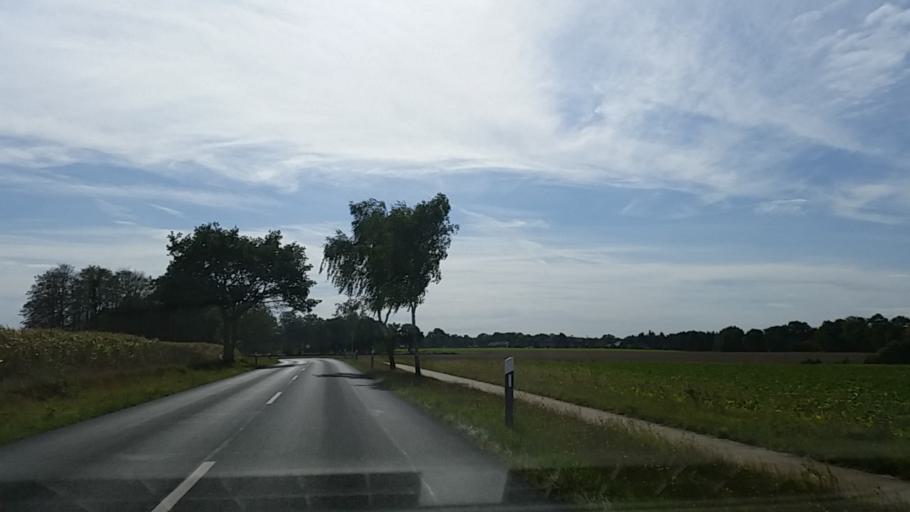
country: DE
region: Lower Saxony
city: Embsen
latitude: 53.1874
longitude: 10.3468
